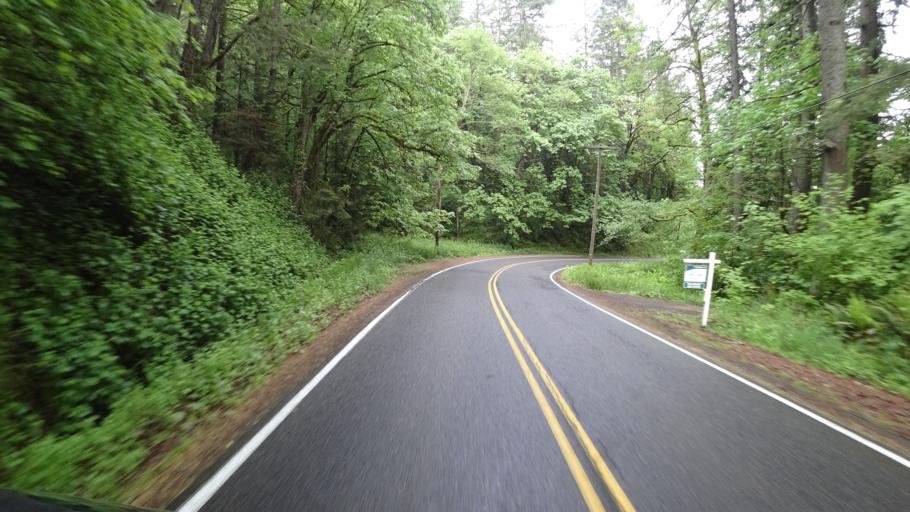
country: US
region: Oregon
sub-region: Washington County
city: West Haven
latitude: 45.5414
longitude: -122.7452
